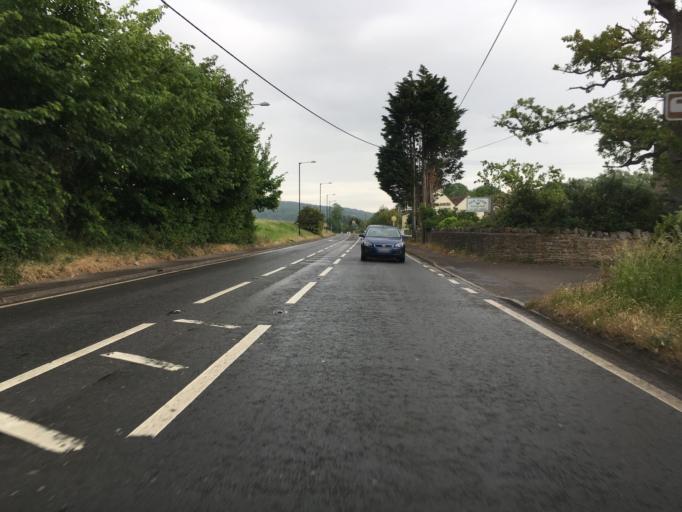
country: GB
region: England
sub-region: North Somerset
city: Congresbury
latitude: 51.3718
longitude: -2.8212
